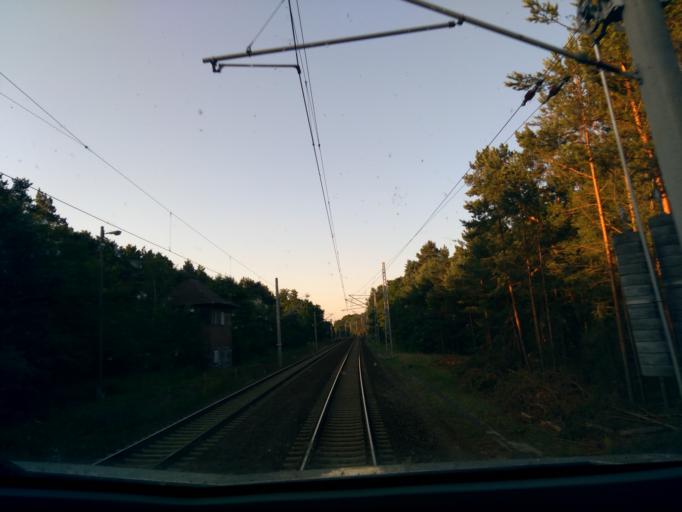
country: DE
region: Brandenburg
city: Gross Koris
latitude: 52.1660
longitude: 13.6484
